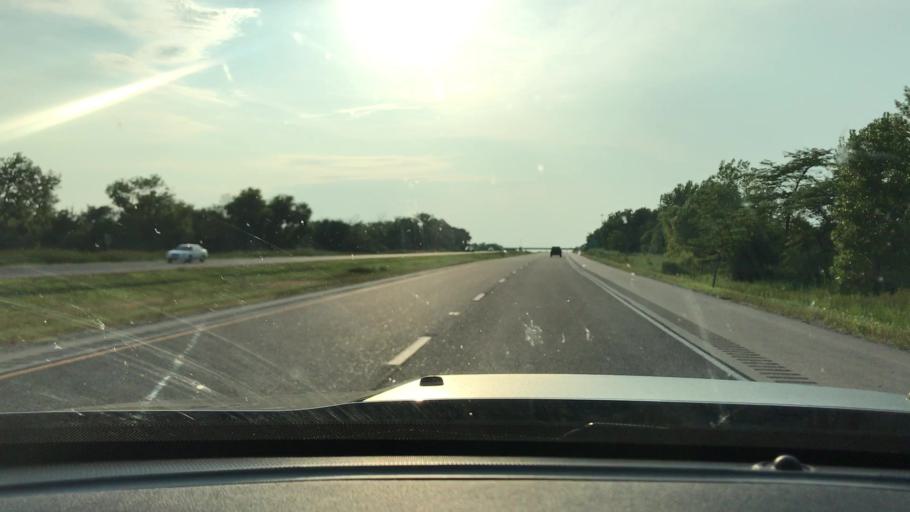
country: US
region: Illinois
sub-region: Henry County
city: Geneseo
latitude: 41.4063
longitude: -90.0057
